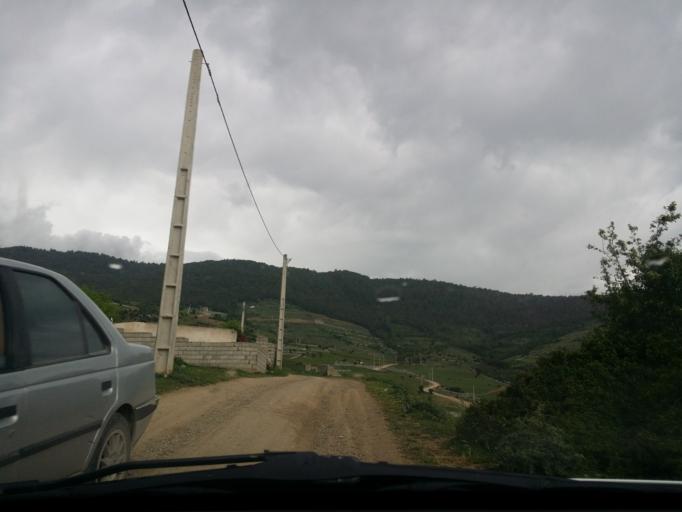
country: IR
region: Mazandaran
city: `Abbasabad
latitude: 36.5071
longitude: 51.1404
